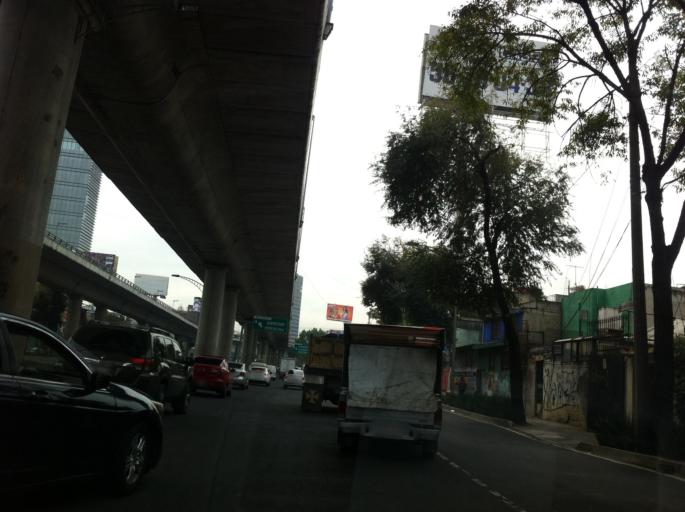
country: MX
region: Mexico City
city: Alvaro Obregon
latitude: 19.3655
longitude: -99.1910
